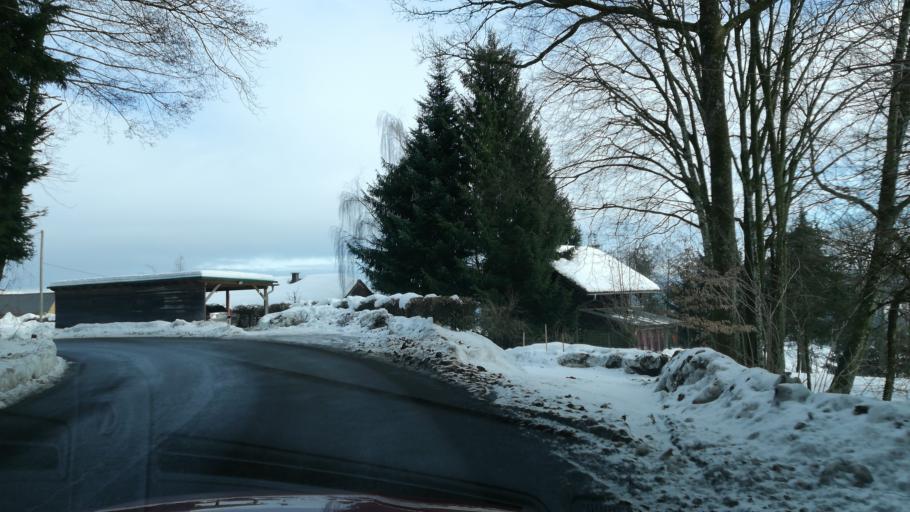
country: AT
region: Upper Austria
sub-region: Politischer Bezirk Vocklabruck
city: Wolfsegg am Hausruck
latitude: 48.1470
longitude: 13.6179
